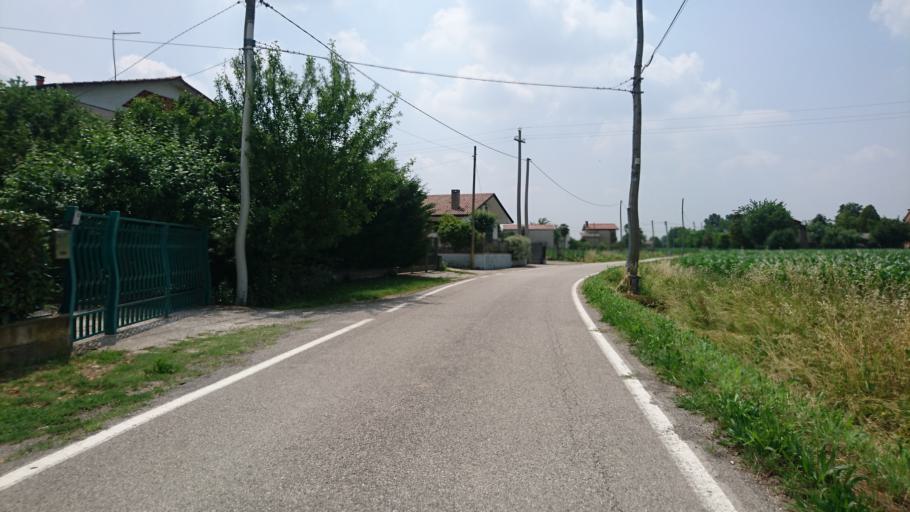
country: IT
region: Veneto
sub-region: Provincia di Padova
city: Cartura
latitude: 45.2647
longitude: 11.8803
